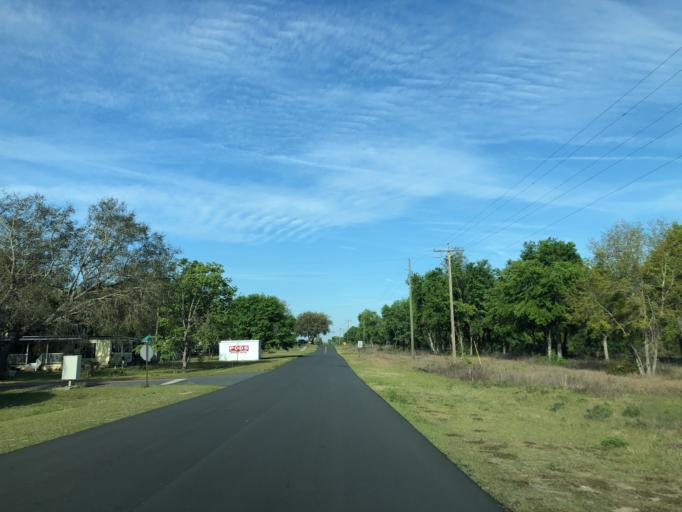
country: US
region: Florida
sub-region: Lake County
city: Astatula
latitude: 28.7210
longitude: -81.7338
